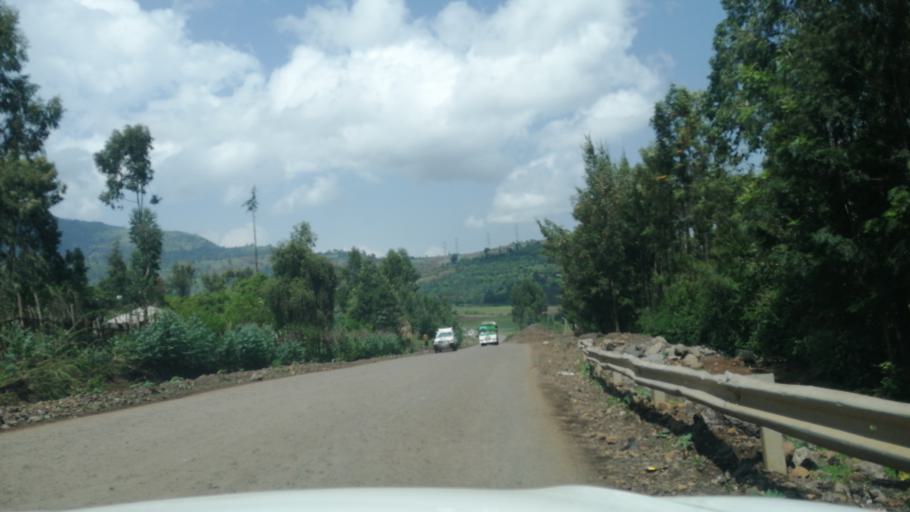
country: ET
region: Oromiya
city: Gedo
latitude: 8.9721
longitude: 37.5849
